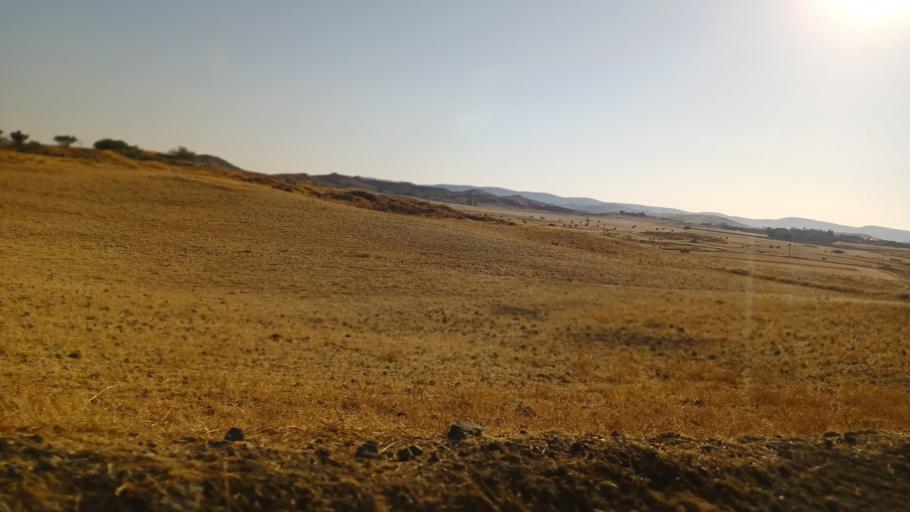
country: CY
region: Larnaka
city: Troulloi
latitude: 35.0129
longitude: 33.5956
